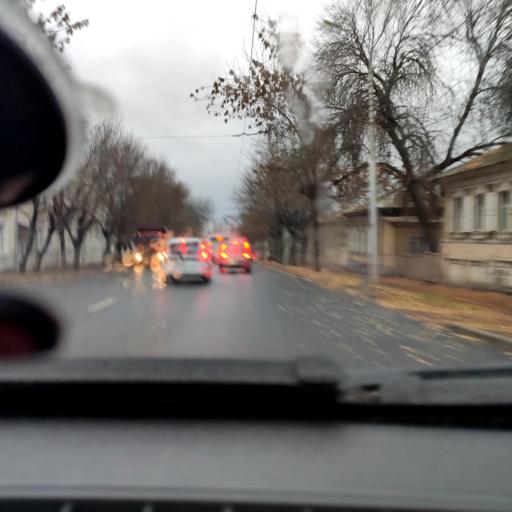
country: RU
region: Bashkortostan
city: Ufa
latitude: 54.7183
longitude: 55.9597
